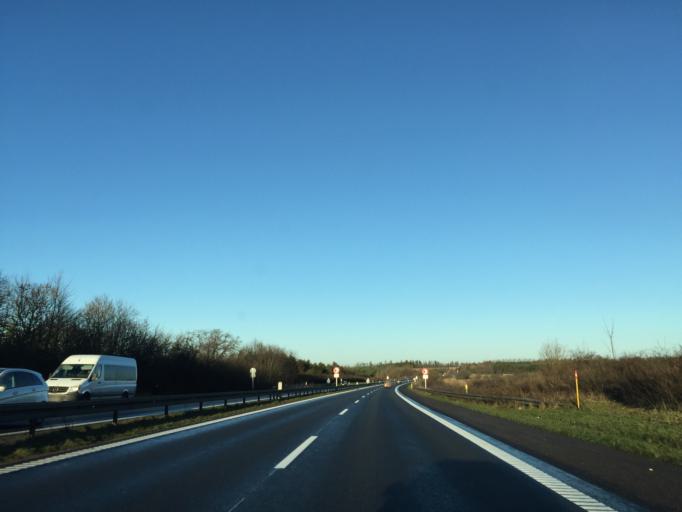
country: DK
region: Central Jutland
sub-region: Skanderborg Kommune
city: Skanderborg
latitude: 55.9956
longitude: 9.8684
